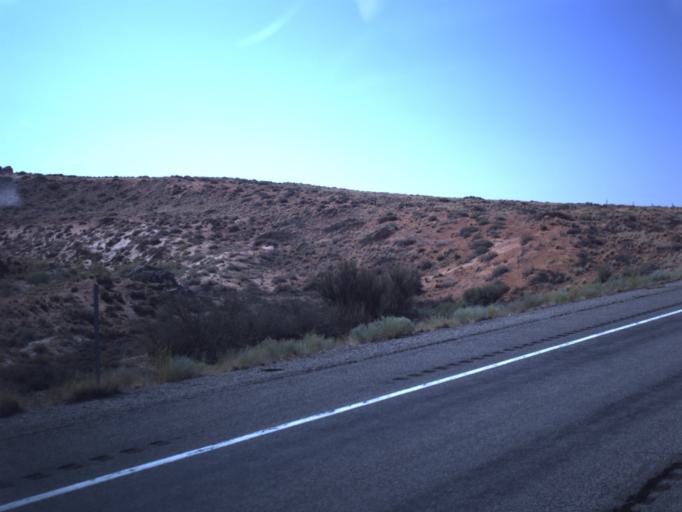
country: US
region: Utah
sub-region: San Juan County
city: Blanding
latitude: 37.2343
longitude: -109.6124
